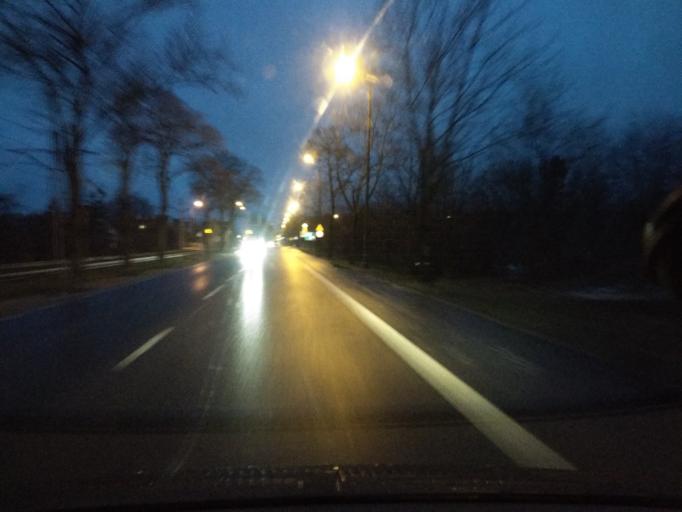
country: PL
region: Lower Silesian Voivodeship
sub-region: Powiat wroclawski
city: Smolec
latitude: 51.1437
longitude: 16.8918
